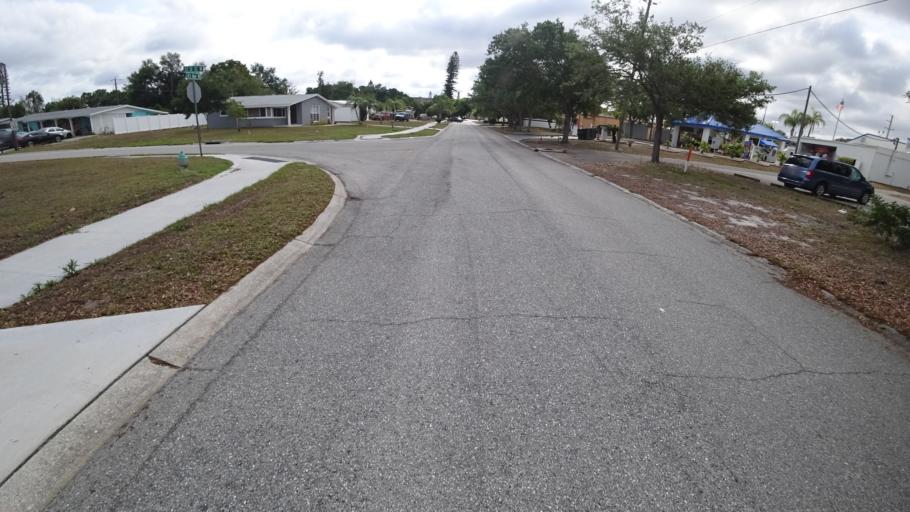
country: US
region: Florida
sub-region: Manatee County
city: South Bradenton
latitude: 27.4635
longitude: -82.6141
